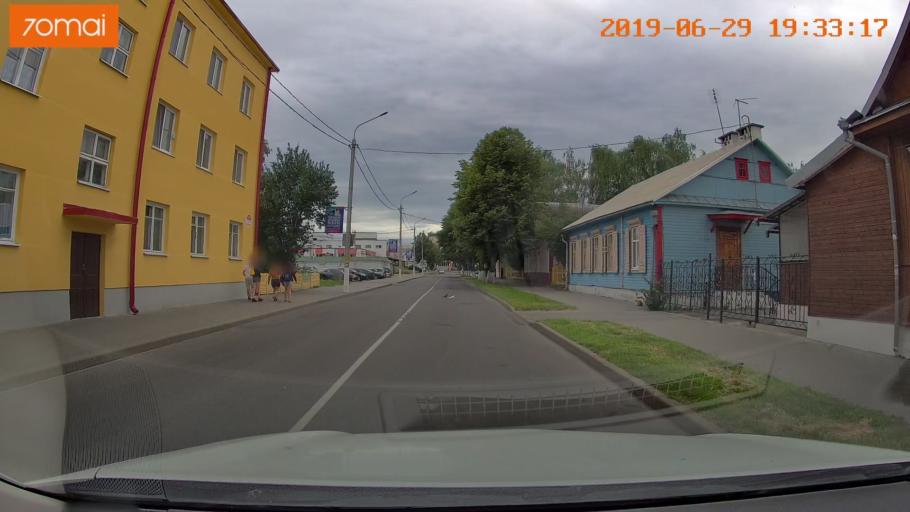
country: BY
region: Brest
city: Pinsk
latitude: 52.1138
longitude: 26.1075
